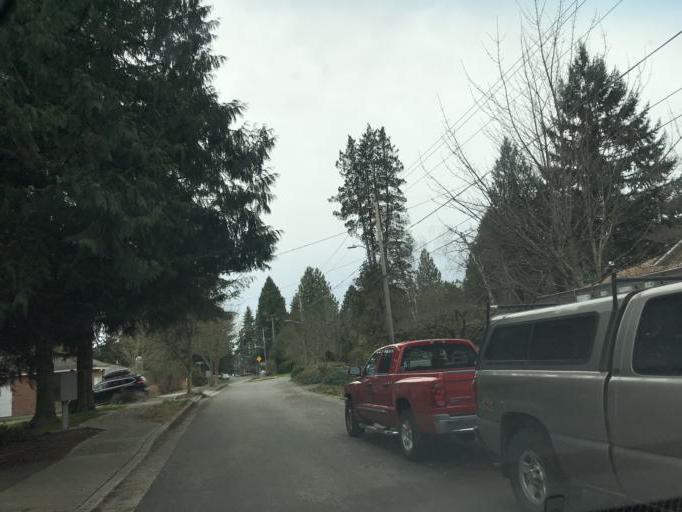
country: US
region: Washington
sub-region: King County
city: Lake Forest Park
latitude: 47.7110
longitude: -122.3062
